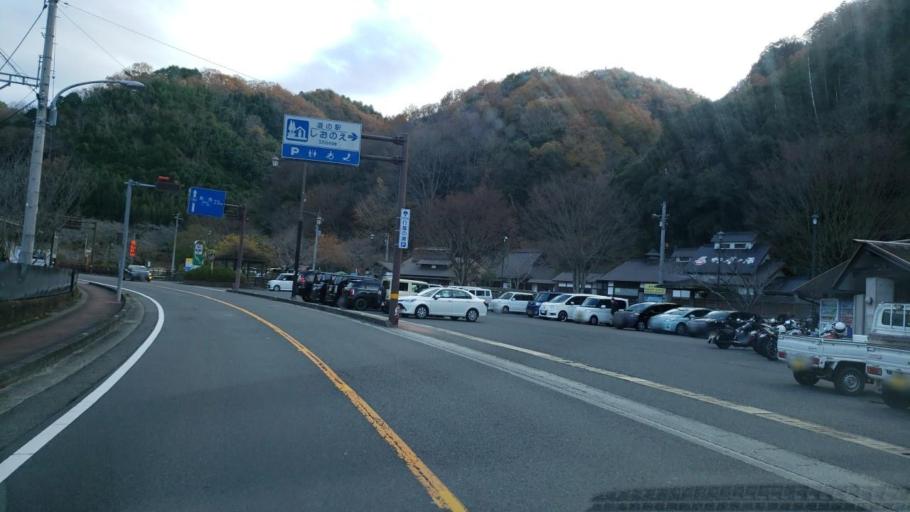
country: JP
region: Tokushima
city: Wakimachi
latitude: 34.1702
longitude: 134.0822
